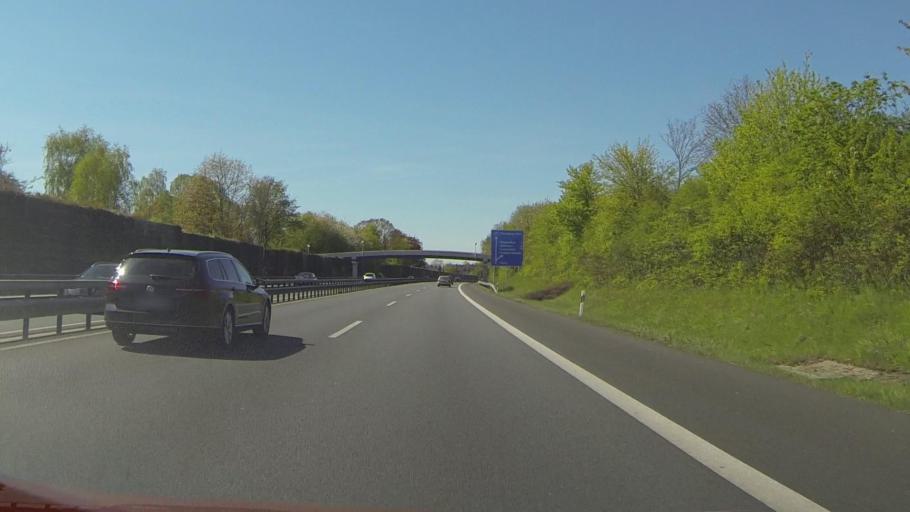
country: DE
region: Schleswig-Holstein
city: Halstenbek
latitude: 53.6346
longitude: 9.8534
